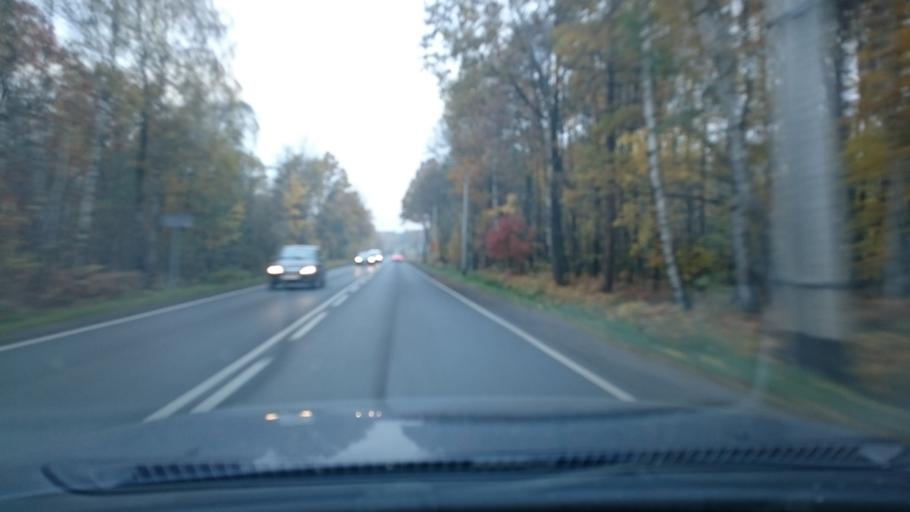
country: PL
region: Silesian Voivodeship
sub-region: Powiat rybnicki
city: Ksiazenice
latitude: 50.1217
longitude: 18.6218
